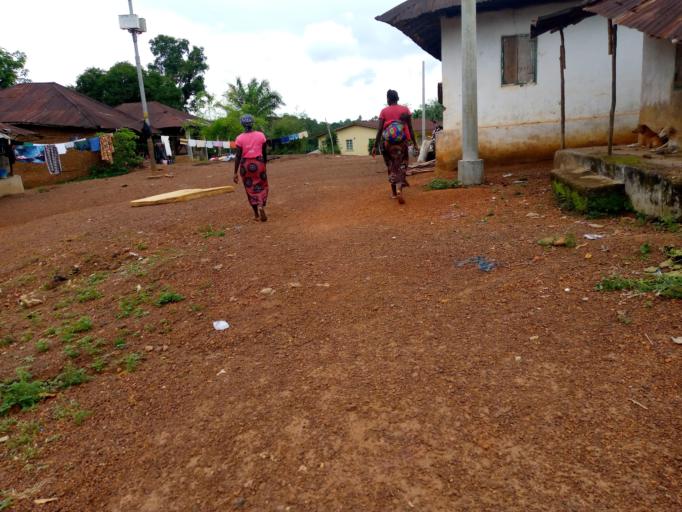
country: SL
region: Southern Province
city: Moyamba
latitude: 8.1561
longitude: -12.4309
